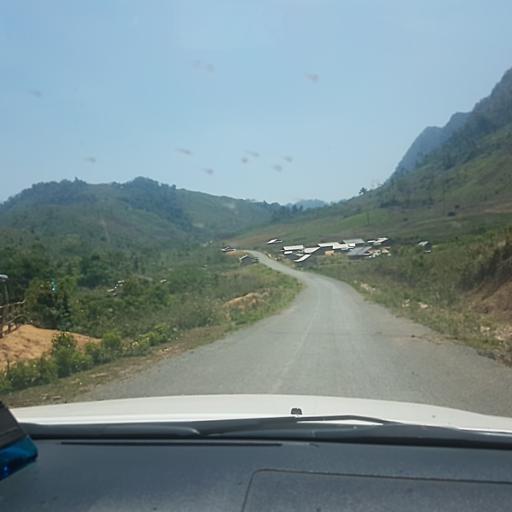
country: VN
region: Nghe An
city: Con Cuong
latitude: 18.5923
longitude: 104.6366
